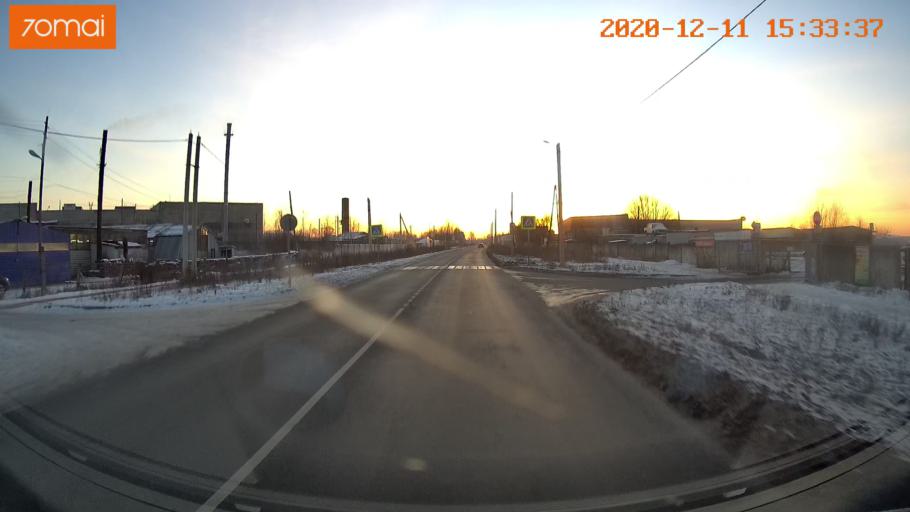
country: RU
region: Ivanovo
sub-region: Gorod Ivanovo
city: Ivanovo
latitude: 57.0508
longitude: 40.9462
